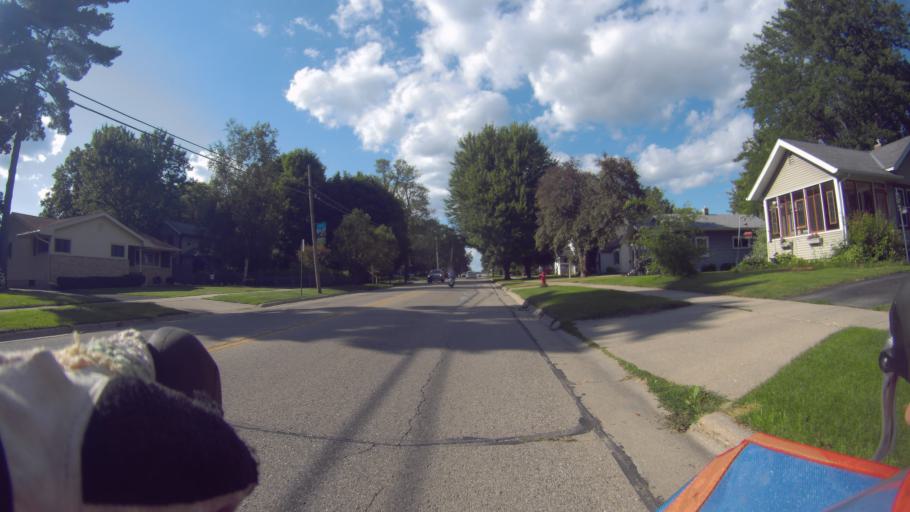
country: US
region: Wisconsin
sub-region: Dane County
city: Oregon
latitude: 42.9328
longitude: -89.3835
